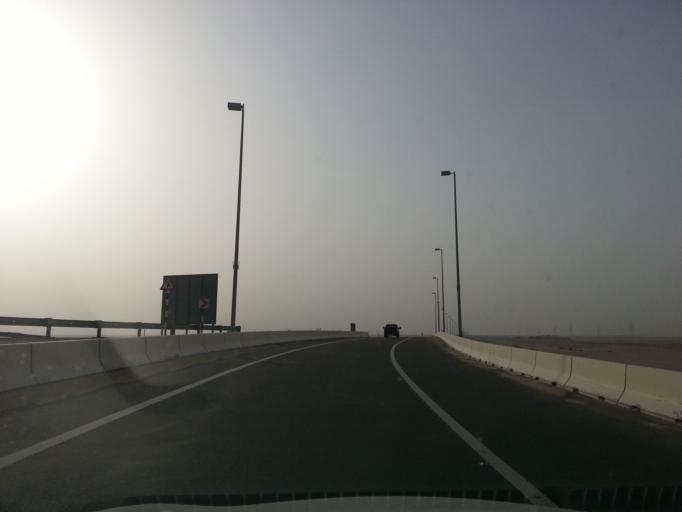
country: AE
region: Dubai
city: Dubai
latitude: 24.7939
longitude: 55.0762
